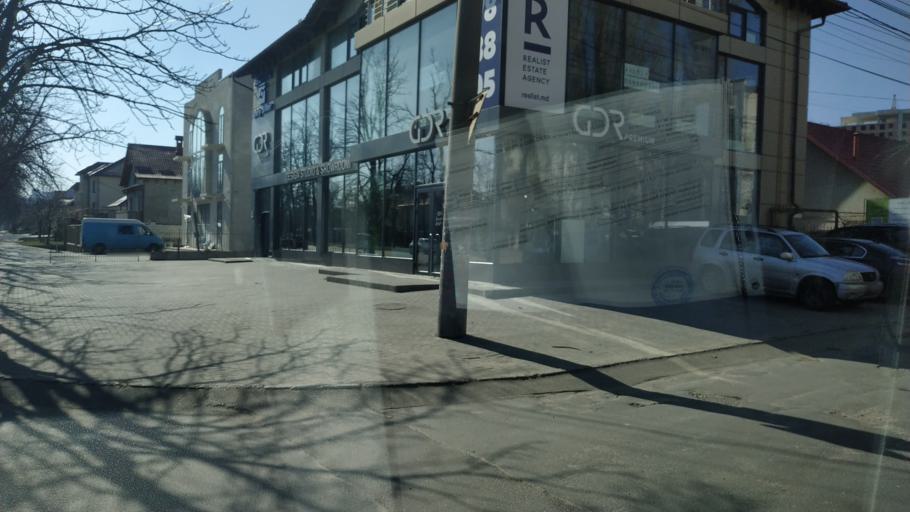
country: MD
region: Chisinau
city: Chisinau
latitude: 47.0282
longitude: 28.8022
